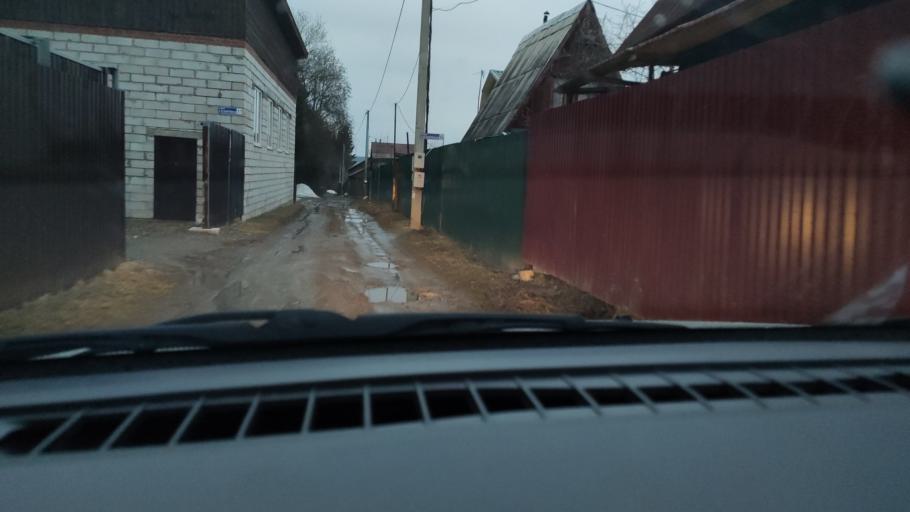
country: RU
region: Perm
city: Polazna
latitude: 58.1798
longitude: 56.4165
